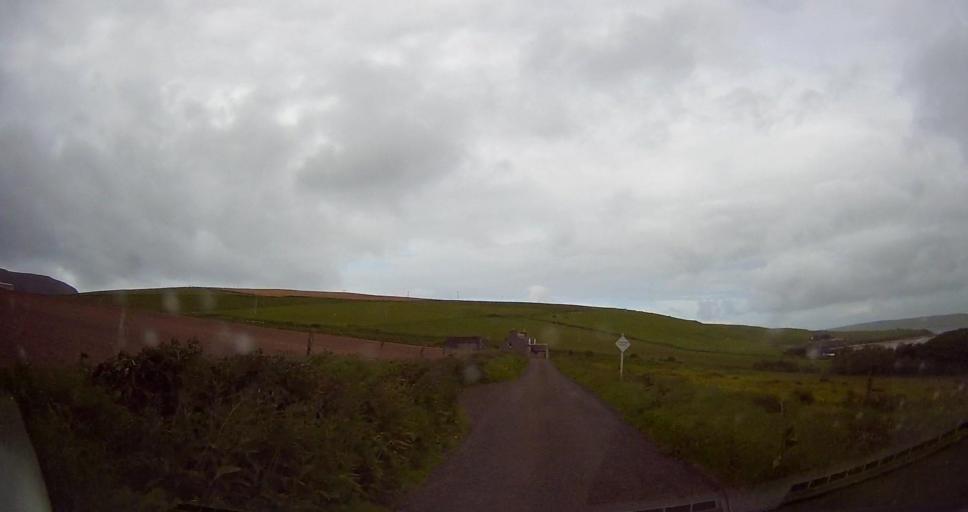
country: GB
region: Scotland
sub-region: Orkney Islands
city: Stromness
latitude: 58.9146
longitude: -3.3250
